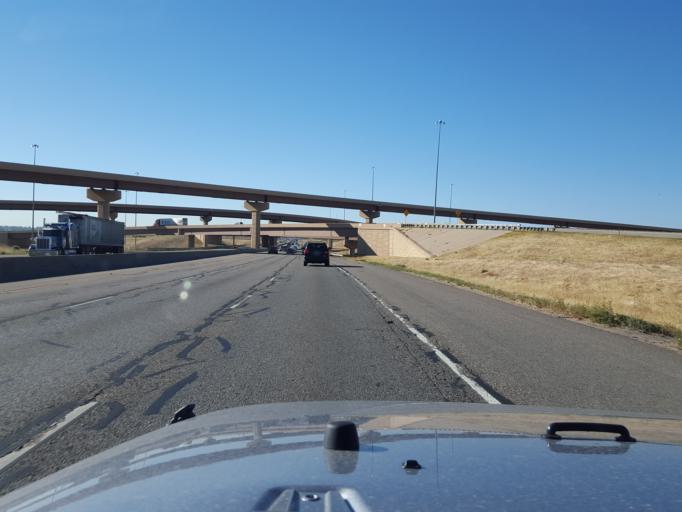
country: US
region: Colorado
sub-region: Boulder County
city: Erie
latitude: 39.9844
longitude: -104.9883
